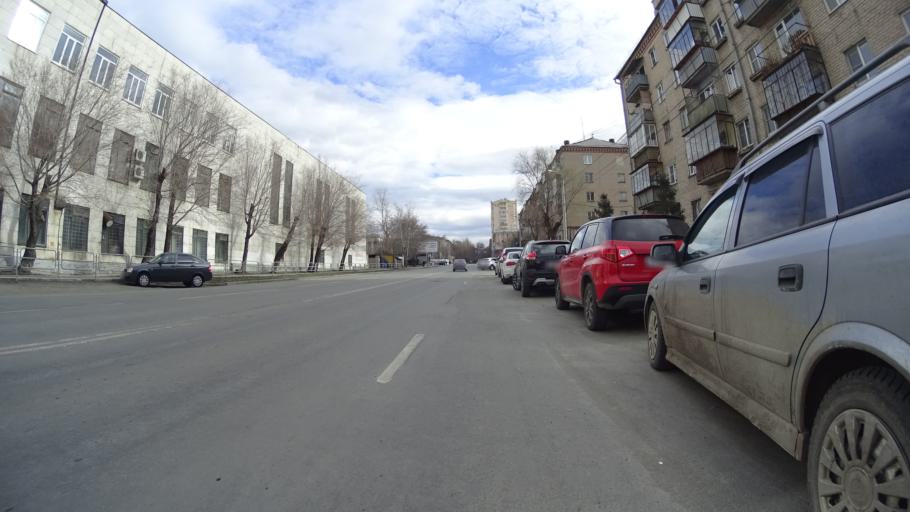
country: RU
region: Chelyabinsk
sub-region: Gorod Chelyabinsk
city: Chelyabinsk
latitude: 55.1618
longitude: 61.3862
